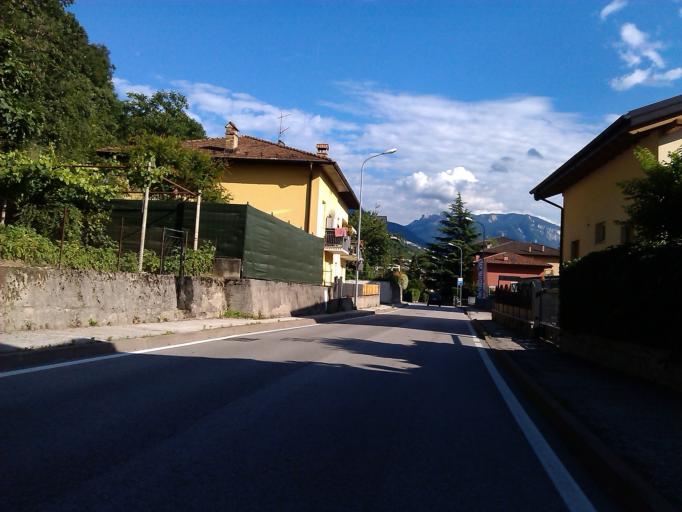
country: IT
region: Trentino-Alto Adige
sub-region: Provincia di Trento
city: Meano
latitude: 46.1050
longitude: 11.1170
